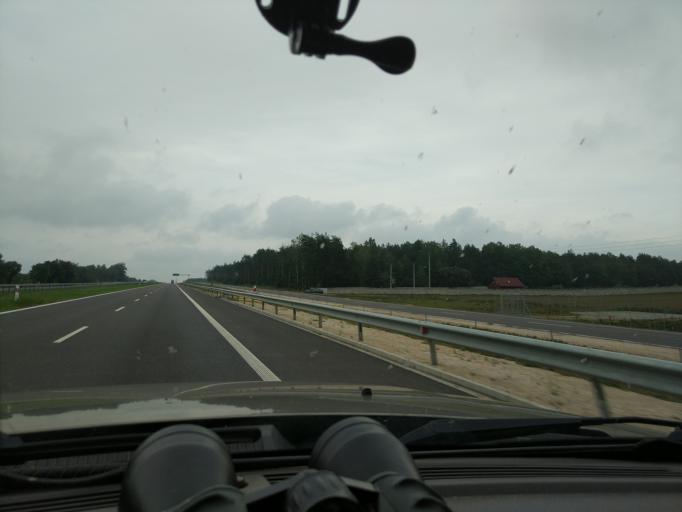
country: PL
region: Podlasie
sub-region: Powiat zambrowski
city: Szumowo
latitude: 52.8986
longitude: 22.0762
